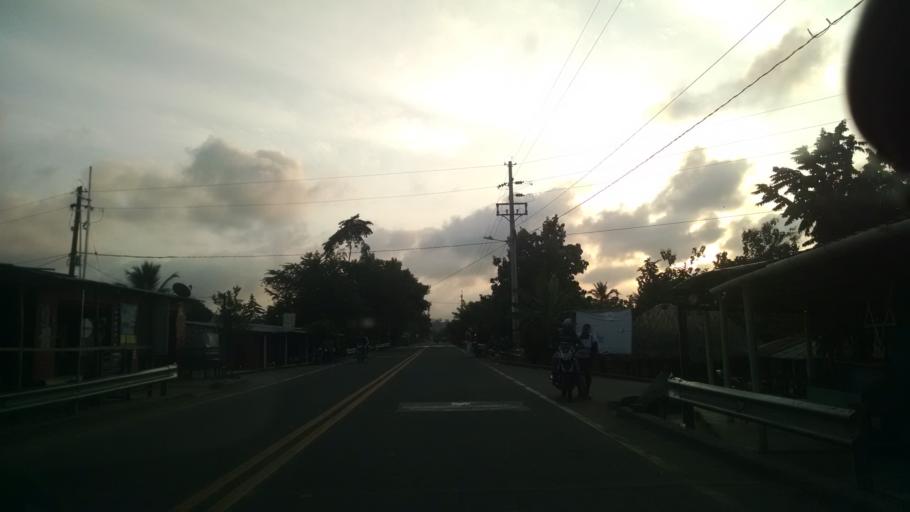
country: CO
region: Antioquia
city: San Juan de Uraba
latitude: 8.7182
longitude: -76.5984
